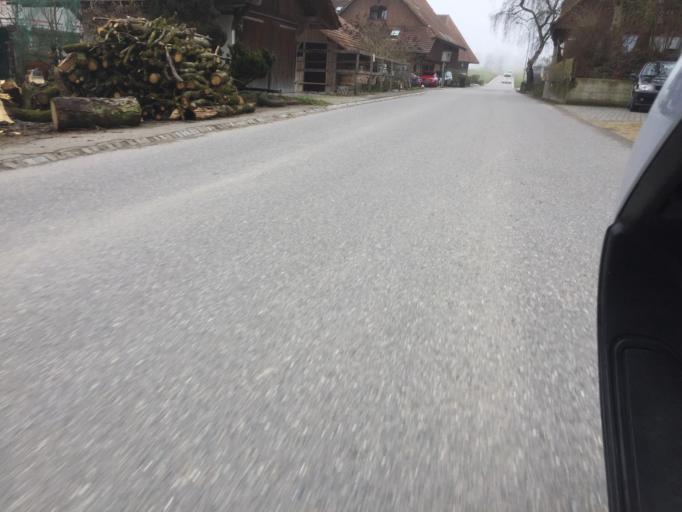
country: CH
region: Bern
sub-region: Seeland District
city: Grossaffoltern
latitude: 47.0857
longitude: 7.3781
